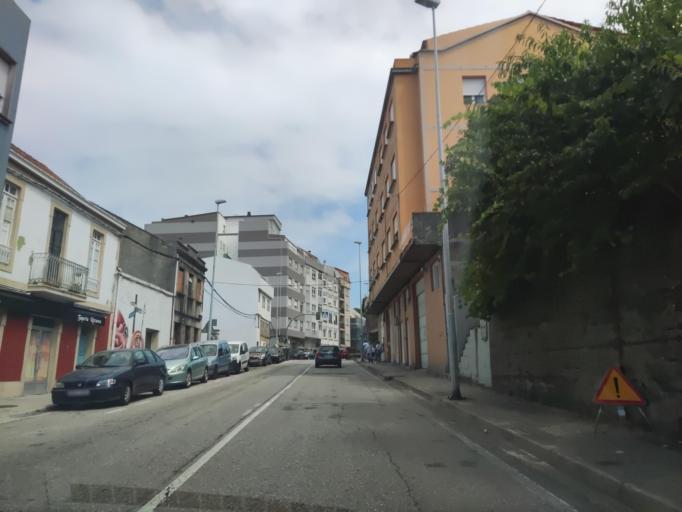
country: ES
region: Galicia
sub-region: Provincia de Pontevedra
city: Vigo
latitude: 42.2621
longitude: -8.6766
